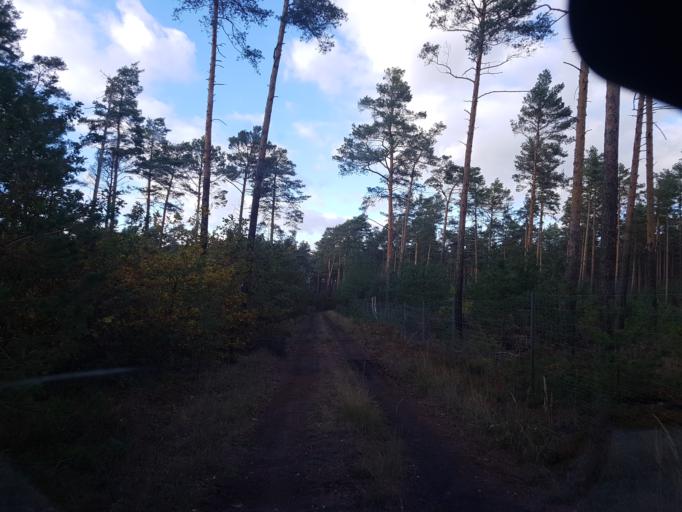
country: DE
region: Brandenburg
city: Finsterwalde
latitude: 51.5538
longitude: 13.7001
